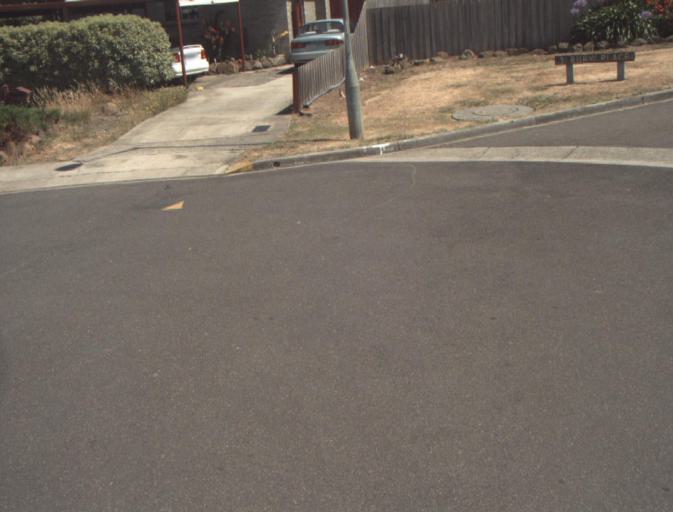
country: AU
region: Tasmania
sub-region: Launceston
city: Newstead
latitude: -41.4147
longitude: 147.1753
